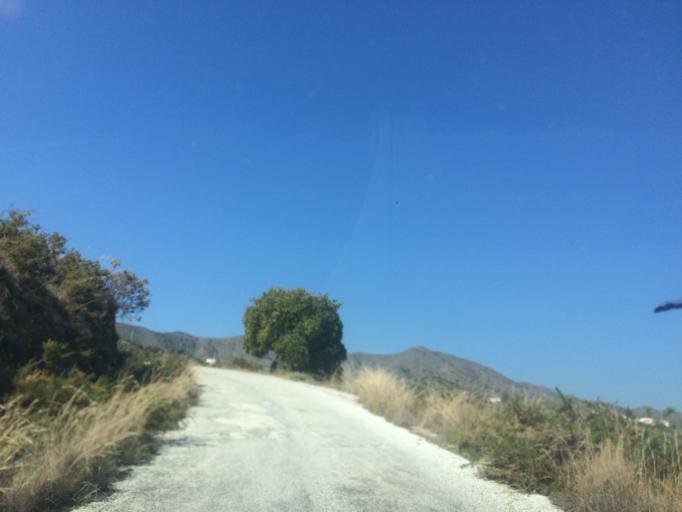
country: ES
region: Andalusia
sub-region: Provincia de Malaga
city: Malaga
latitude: 36.7534
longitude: -4.4381
